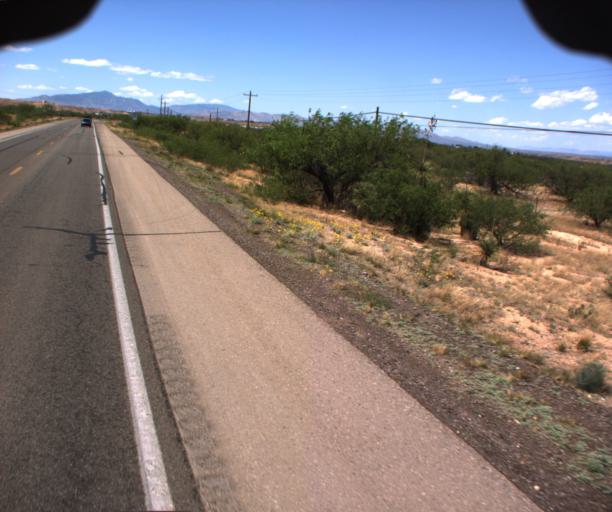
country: US
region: Arizona
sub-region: Cochise County
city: Benson
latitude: 31.9291
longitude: -110.2795
